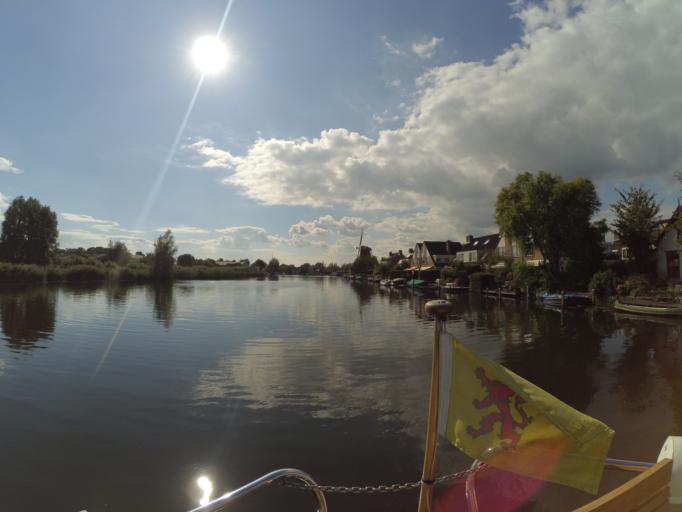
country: NL
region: Utrecht
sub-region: Stichtse Vecht
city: Vreeland
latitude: 52.2352
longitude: 5.0323
